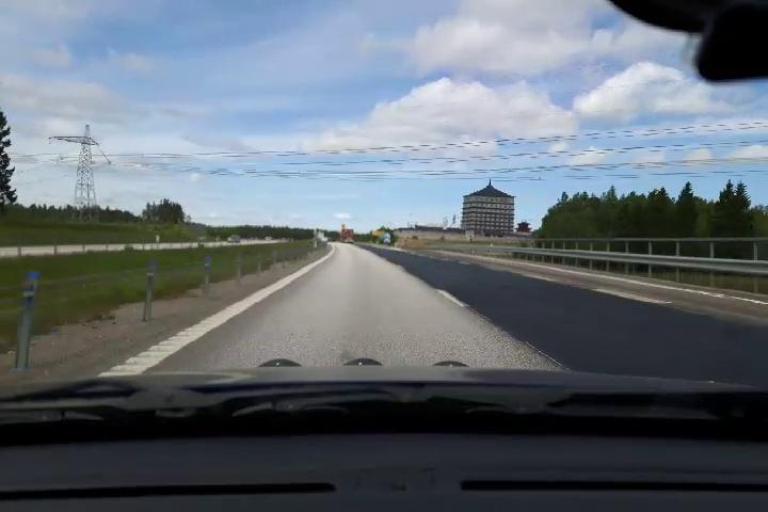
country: SE
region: Uppsala
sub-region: Alvkarleby Kommun
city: AElvkarleby
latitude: 60.4594
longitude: 17.4148
